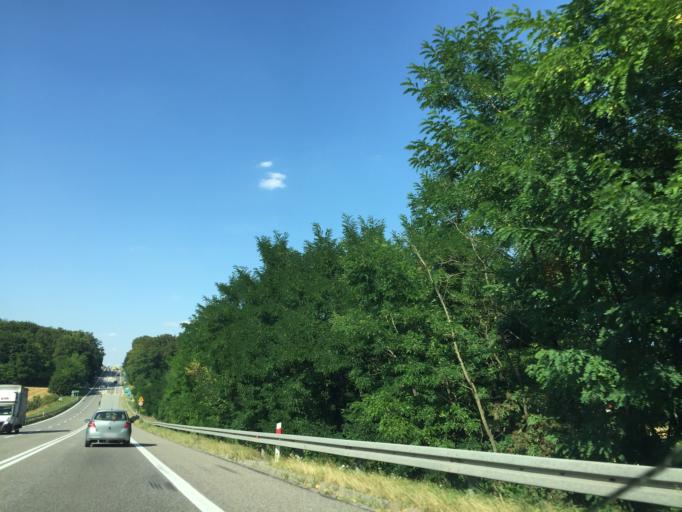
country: PL
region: Swietokrzyskie
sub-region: Powiat jedrzejowski
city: Wodzislaw
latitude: 50.4234
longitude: 20.1273
